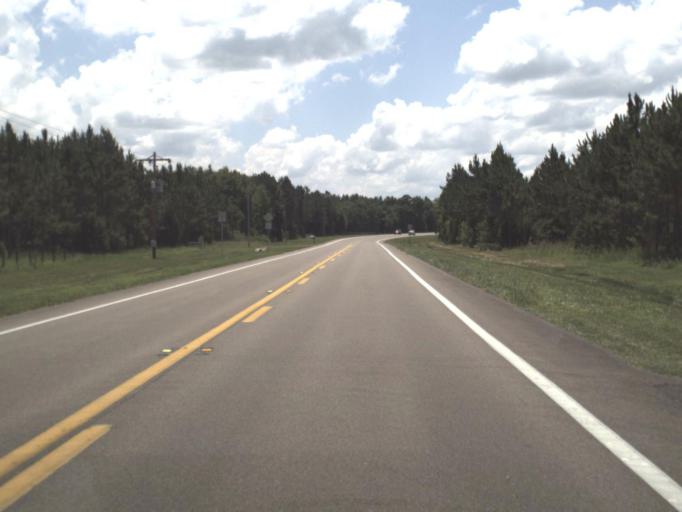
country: US
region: Florida
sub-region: Union County
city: Lake Butler
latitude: 29.9149
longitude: -82.4255
